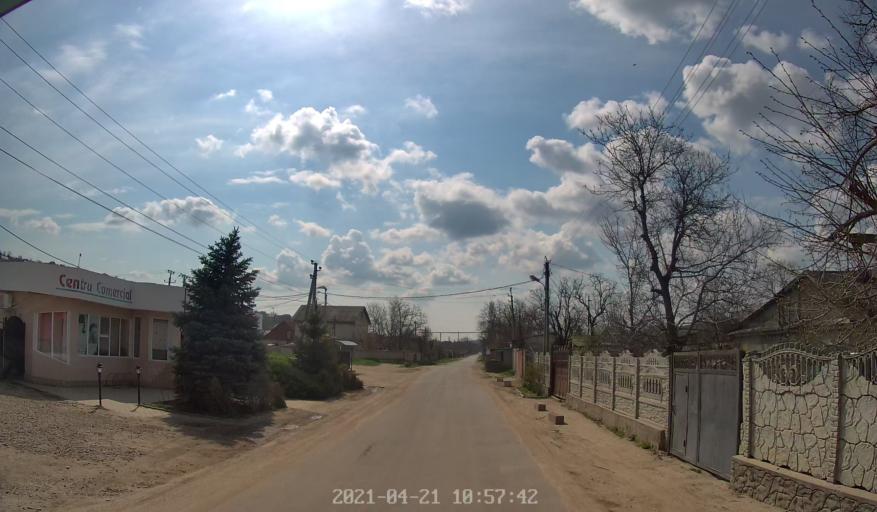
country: MD
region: Chisinau
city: Singera
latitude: 46.9583
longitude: 28.9400
